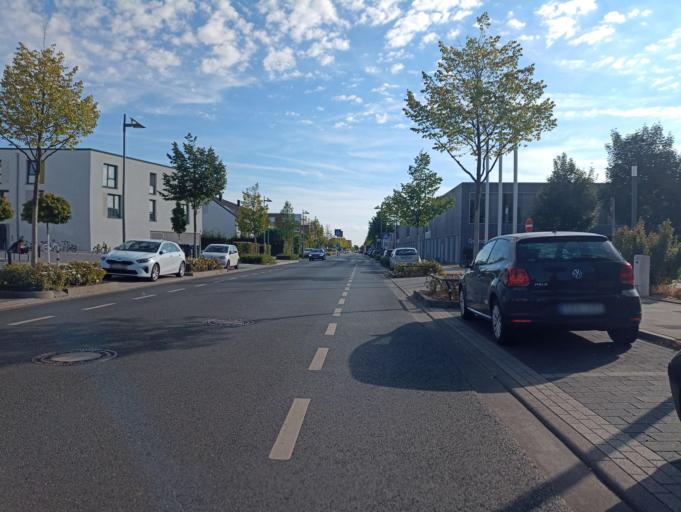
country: DE
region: Hesse
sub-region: Regierungsbezirk Darmstadt
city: Bad Homburg vor der Hoehe
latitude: 50.1799
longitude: 8.6187
